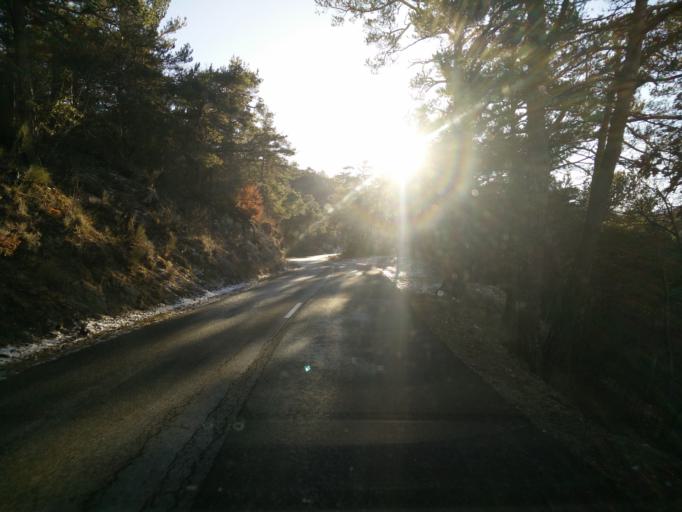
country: FR
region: Provence-Alpes-Cote d'Azur
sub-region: Departement des Alpes-de-Haute-Provence
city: Castellane
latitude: 43.7889
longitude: 6.3761
